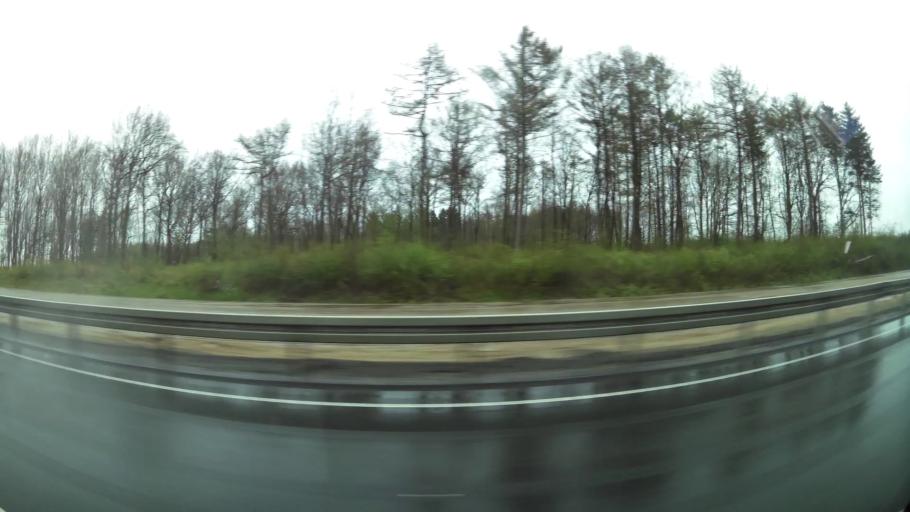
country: DK
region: Central Jutland
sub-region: Herning Kommune
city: Avlum
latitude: 56.2229
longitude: 8.8363
